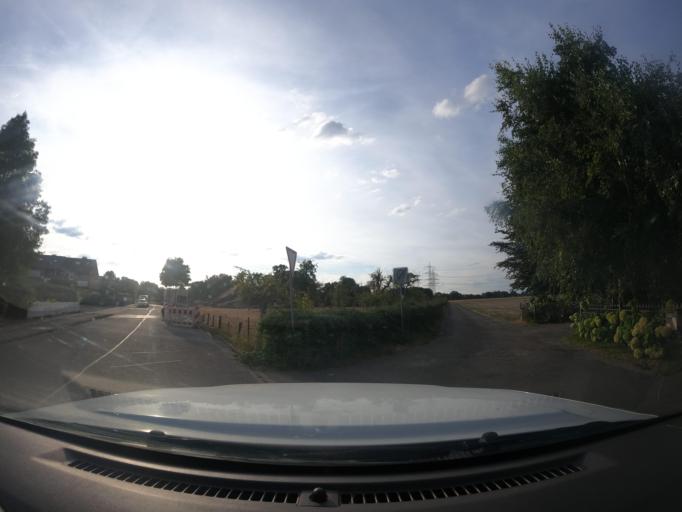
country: DE
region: North Rhine-Westphalia
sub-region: Regierungsbezirk Dusseldorf
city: Wesel
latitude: 51.6970
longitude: 6.6100
